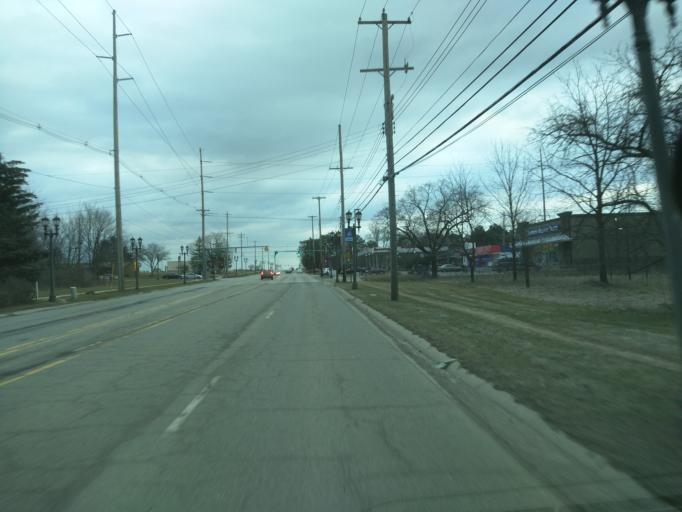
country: US
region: Michigan
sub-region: Ingham County
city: Lansing
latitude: 42.7607
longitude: -84.5246
